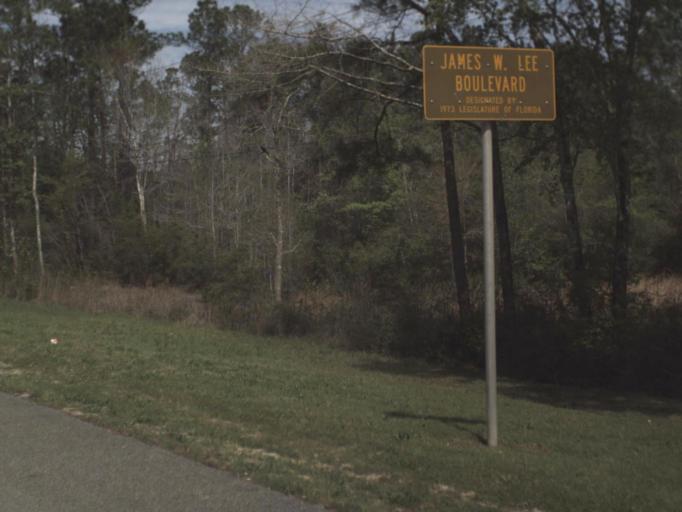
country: US
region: Florida
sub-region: Okaloosa County
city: Crestview
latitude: 30.7539
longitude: -86.5146
